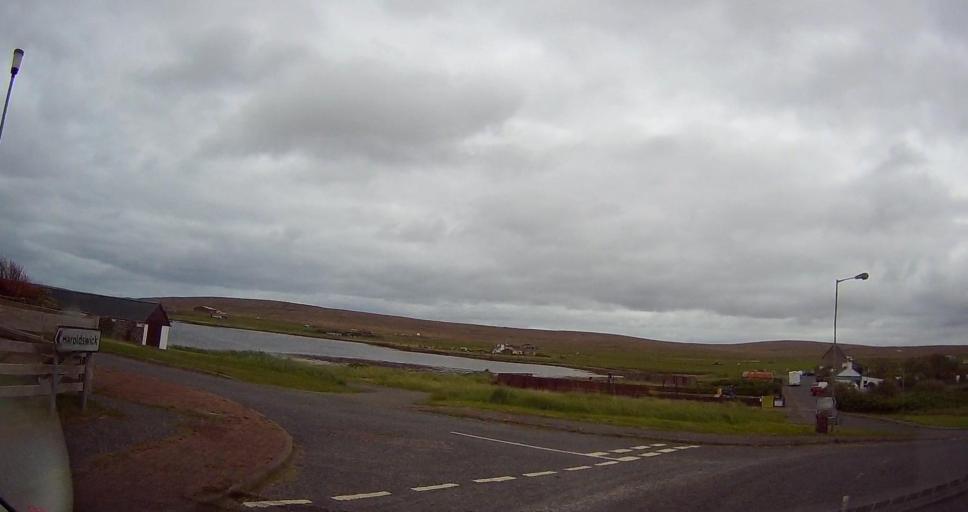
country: GB
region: Scotland
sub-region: Shetland Islands
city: Shetland
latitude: 60.7586
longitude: -0.8590
